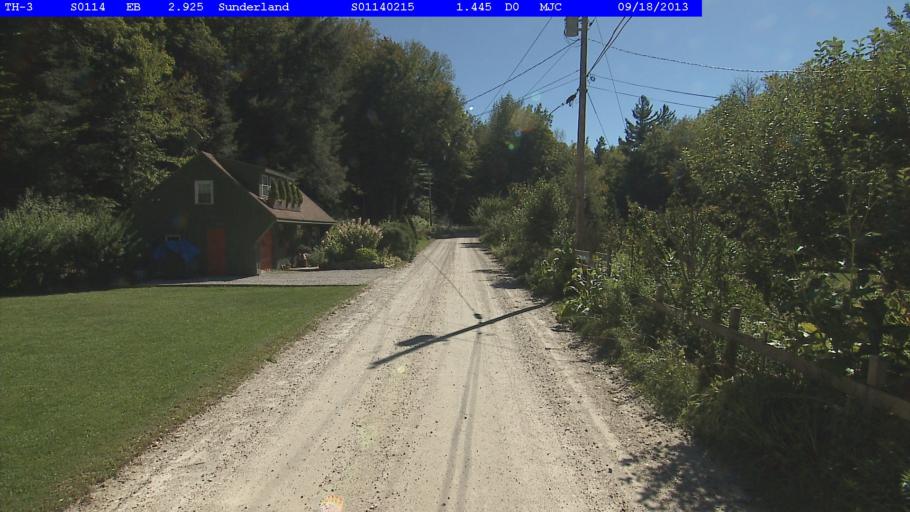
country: US
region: Vermont
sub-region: Bennington County
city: Arlington
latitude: 43.0526
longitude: -73.1152
